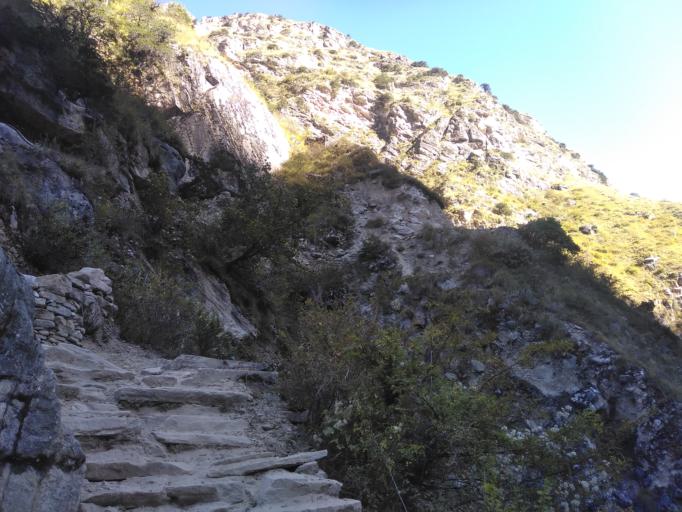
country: NP
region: Western Region
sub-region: Dhawalagiri Zone
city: Jomsom
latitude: 28.9330
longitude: 83.0474
